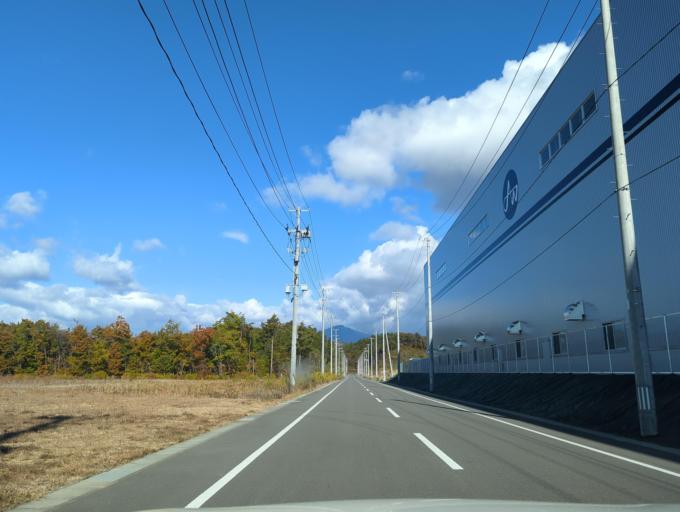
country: JP
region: Fukushima
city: Koriyama
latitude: 37.4586
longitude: 140.2975
